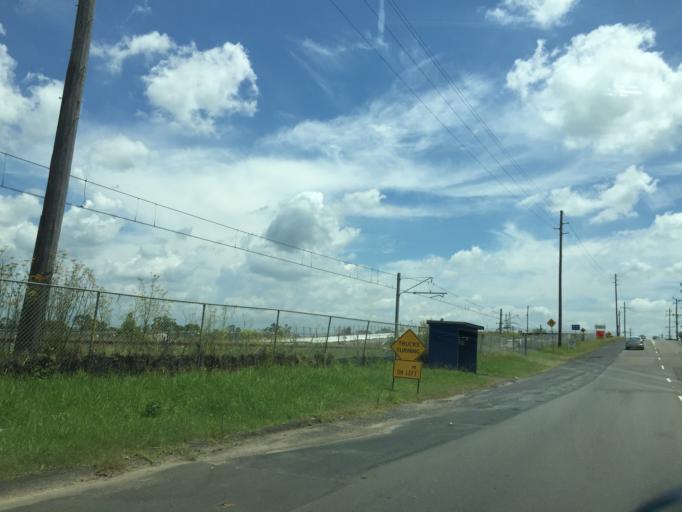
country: AU
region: New South Wales
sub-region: Blacktown
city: Riverstone
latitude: -33.6943
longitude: 150.8687
